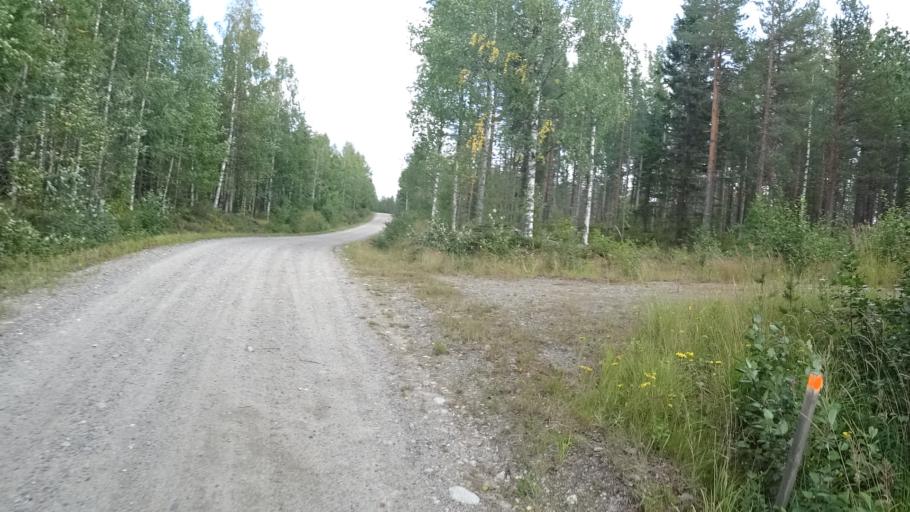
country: FI
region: North Karelia
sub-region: Joensuu
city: Ilomantsi
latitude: 62.6192
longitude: 31.2361
